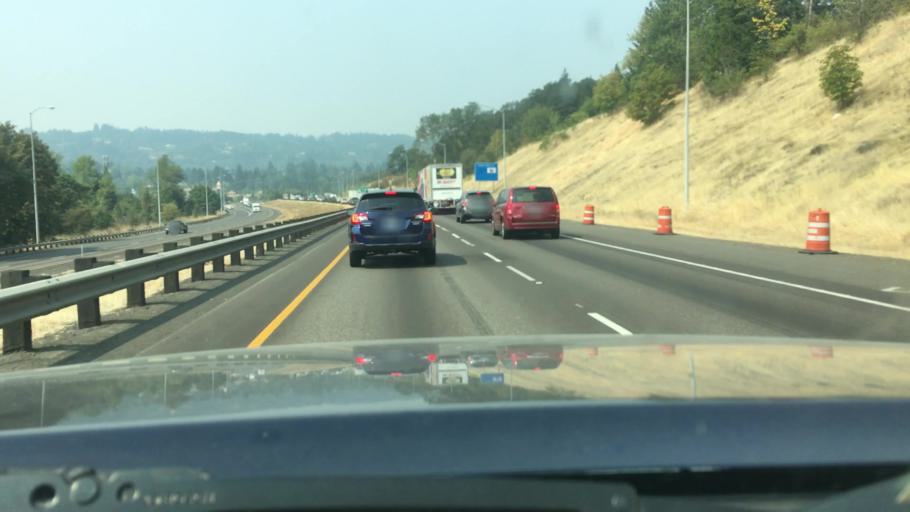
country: US
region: Oregon
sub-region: Clackamas County
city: West Linn
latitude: 45.3490
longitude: -122.6404
